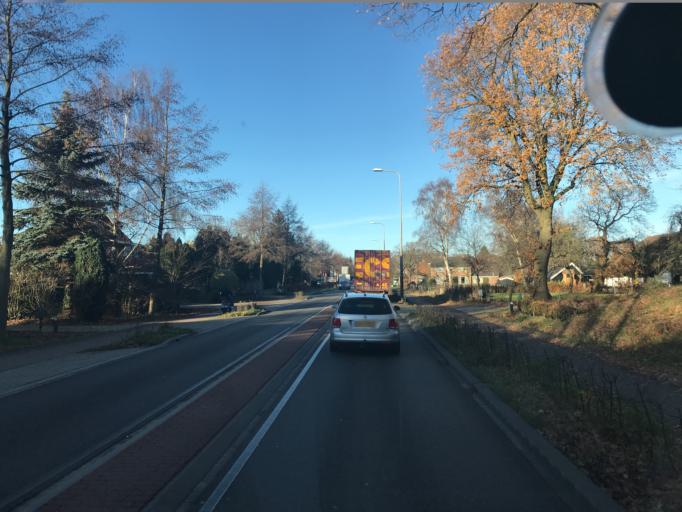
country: NL
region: Gelderland
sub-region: Gemeente Harderwijk
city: Harderwijk
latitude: 52.3206
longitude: 5.6234
